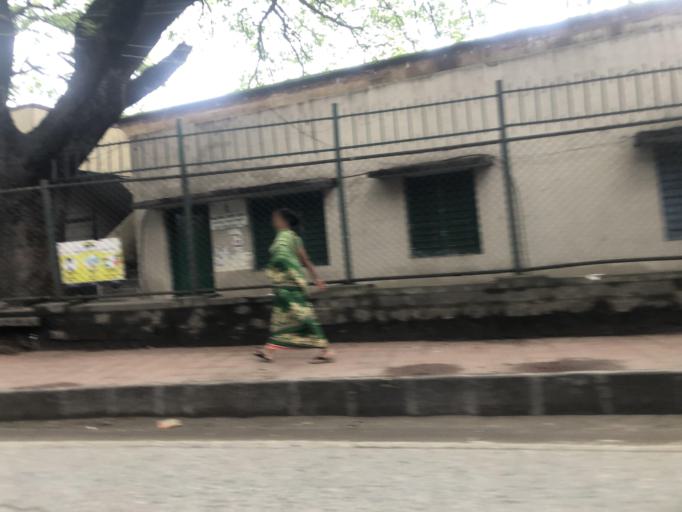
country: IN
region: Karnataka
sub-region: Bangalore Urban
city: Bangalore
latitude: 12.9698
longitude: 77.5671
